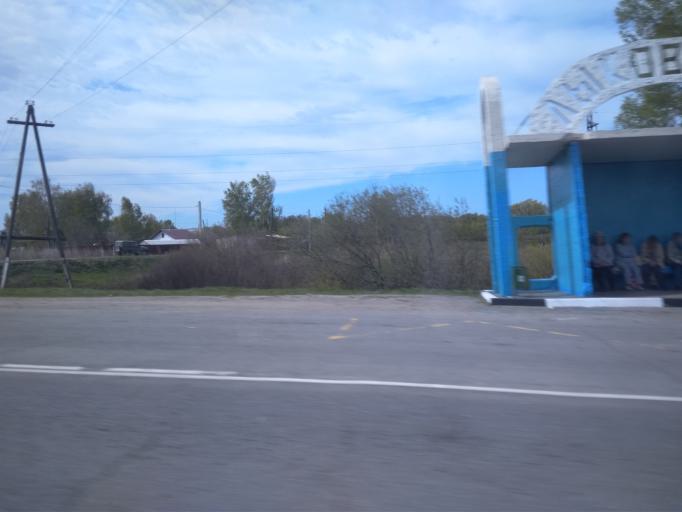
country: RU
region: Mordoviya
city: Atemar
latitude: 54.3183
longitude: 45.4749
